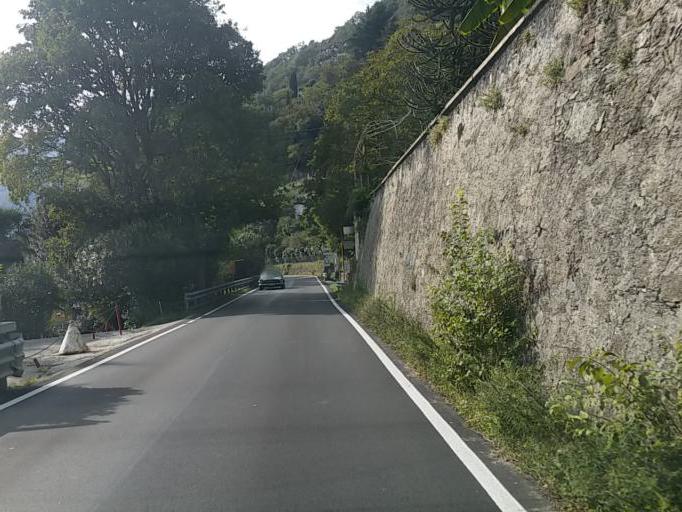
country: IT
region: Piedmont
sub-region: Provincia Verbano-Cusio-Ossola
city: Cannero Riviera
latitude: 46.0254
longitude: 8.7003
